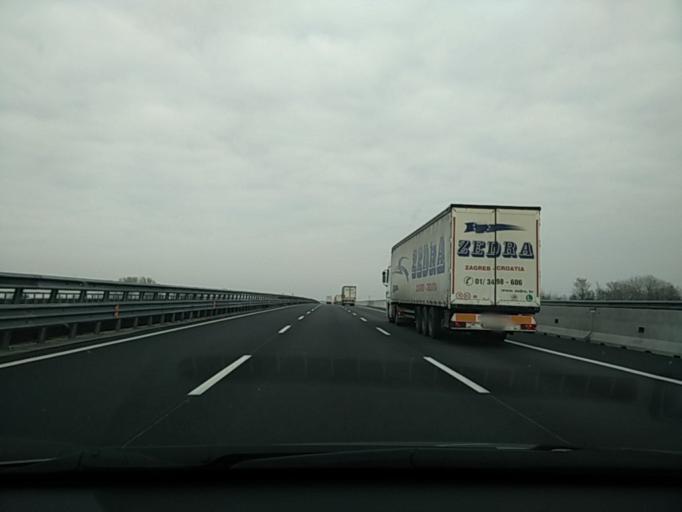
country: IT
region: Veneto
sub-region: Provincia di Venezia
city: Fossalta di Piave
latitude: 45.6635
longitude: 12.5132
